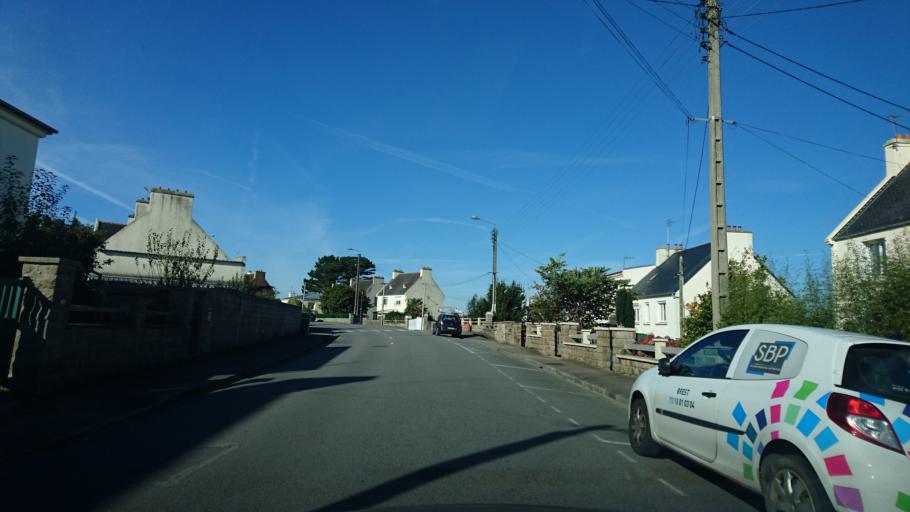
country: FR
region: Brittany
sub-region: Departement du Finistere
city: Saint-Renan
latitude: 48.4327
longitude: -4.6281
